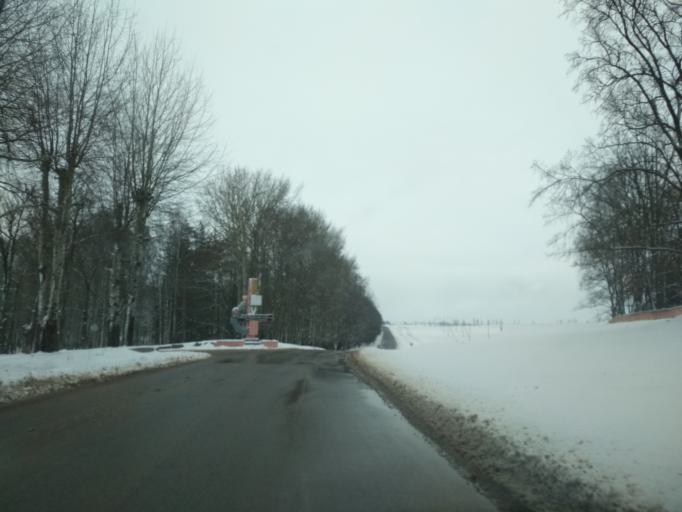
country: BY
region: Minsk
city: Mar''ina Horka
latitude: 53.5290
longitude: 28.1299
